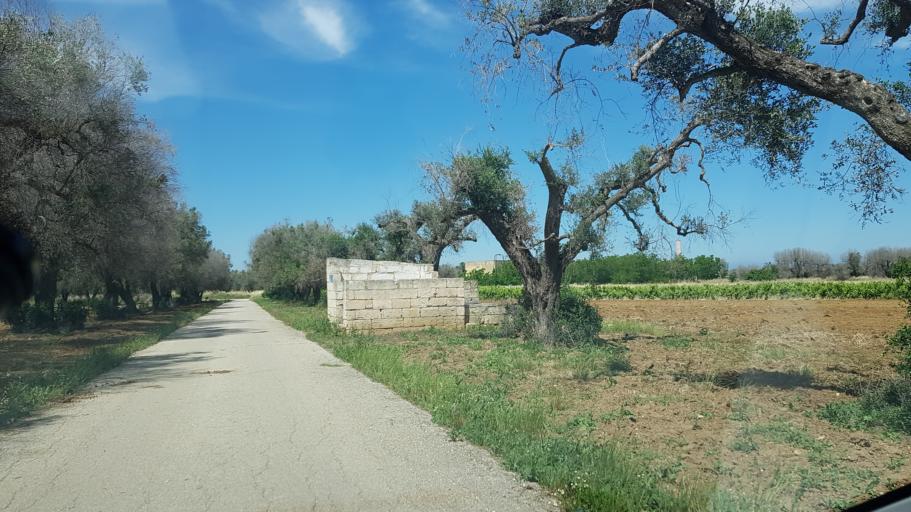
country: IT
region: Apulia
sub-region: Provincia di Brindisi
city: Tuturano
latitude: 40.5409
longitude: 17.9979
